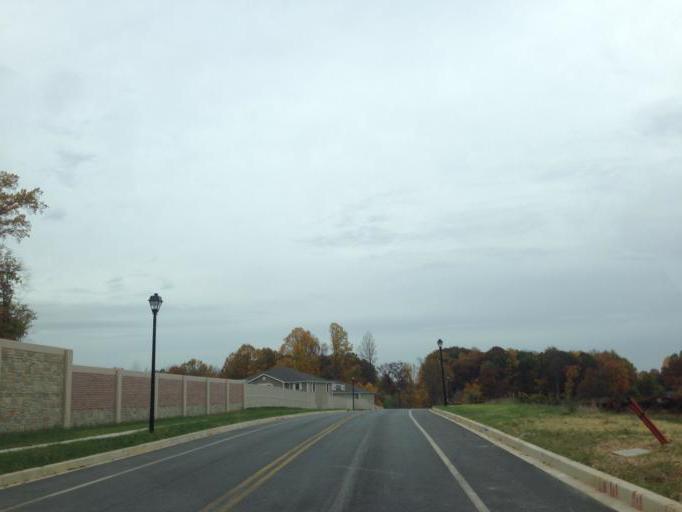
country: US
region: Maryland
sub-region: Howard County
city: Columbia
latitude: 39.3040
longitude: -76.8807
